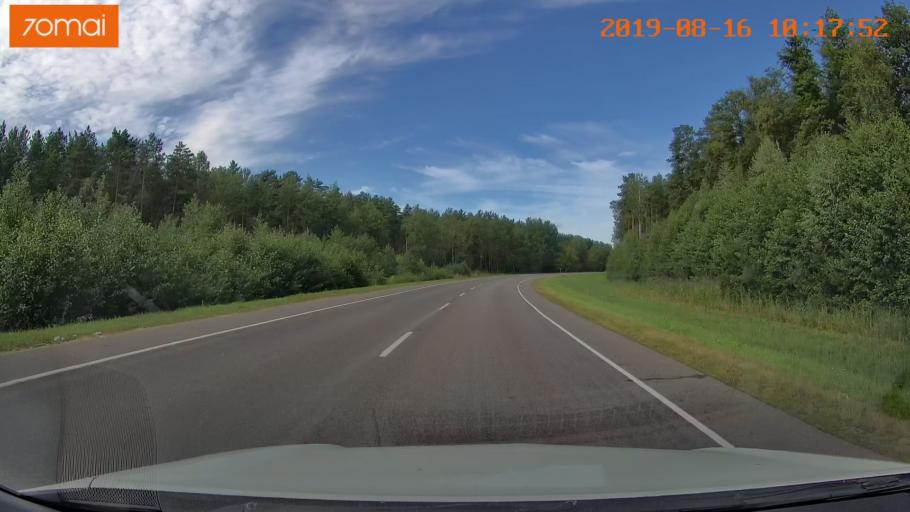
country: BY
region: Mogilev
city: Asipovichy
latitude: 53.3059
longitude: 28.7049
